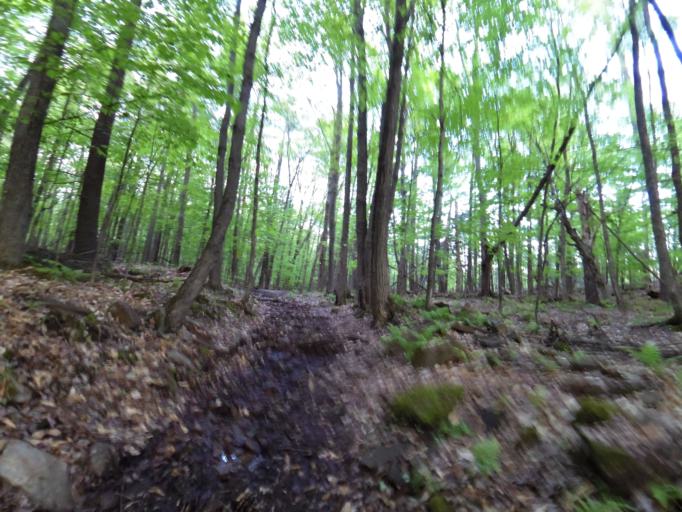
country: CA
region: Ontario
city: Bells Corners
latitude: 45.3366
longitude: -75.8722
